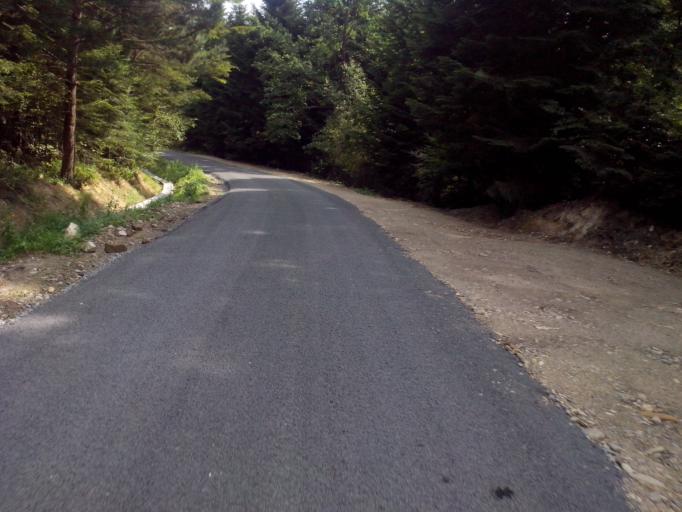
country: PL
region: Subcarpathian Voivodeship
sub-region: Powiat strzyzowski
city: Strzyzow
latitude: 49.8102
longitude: 21.8022
